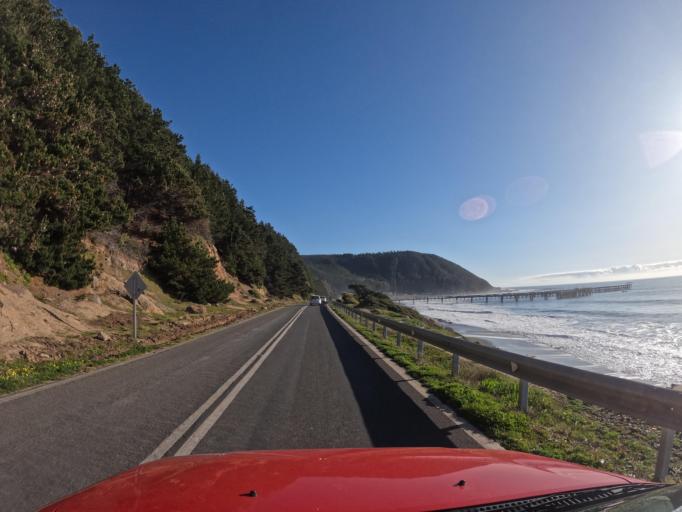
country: CL
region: Maule
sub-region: Provincia de Talca
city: Constitucion
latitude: -35.3545
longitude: -72.4511
